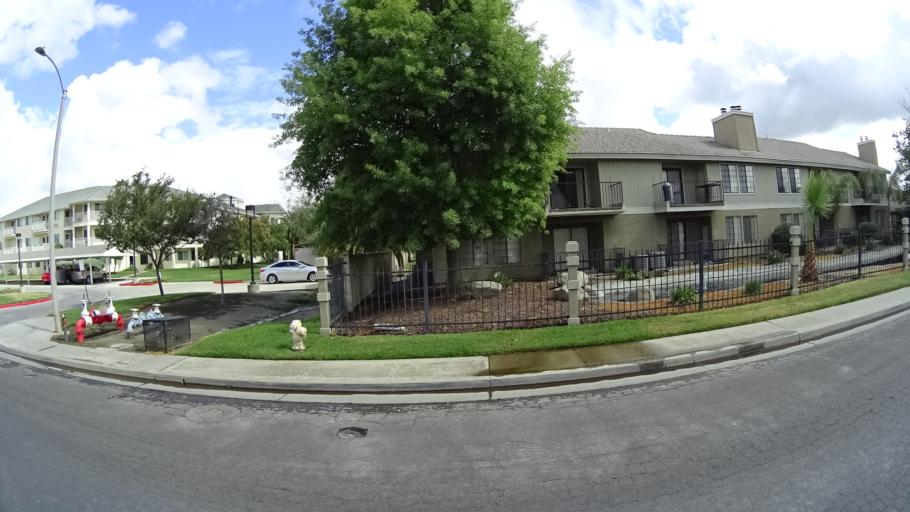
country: US
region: California
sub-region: Kings County
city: Lucerne
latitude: 36.3600
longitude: -119.6538
